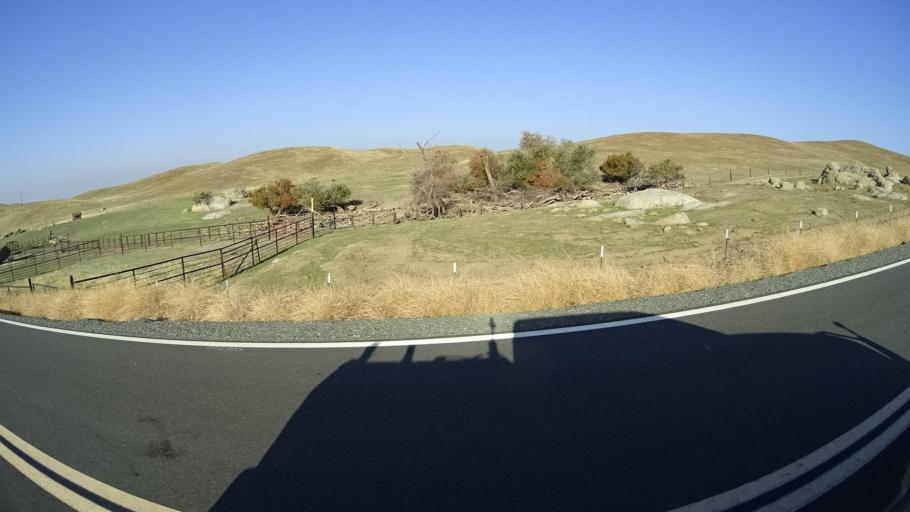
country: US
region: California
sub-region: Tulare County
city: Richgrove
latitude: 35.7429
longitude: -118.8831
